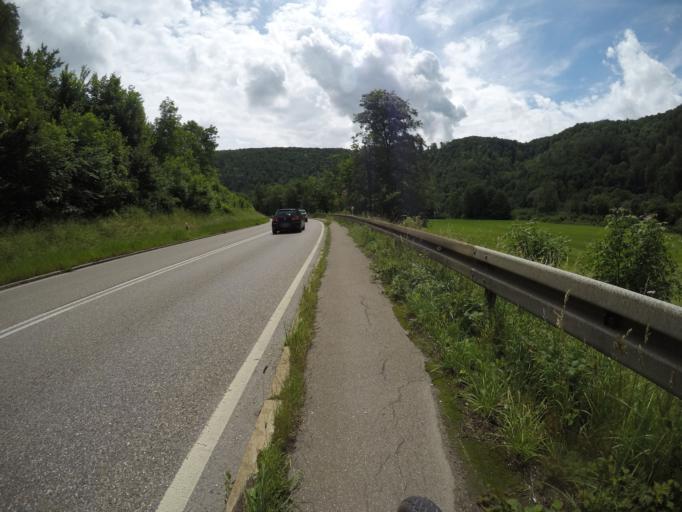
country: DE
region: Baden-Wuerttemberg
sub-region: Regierungsbezirk Stuttgart
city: Geislingen an der Steige
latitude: 48.6008
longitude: 9.8419
